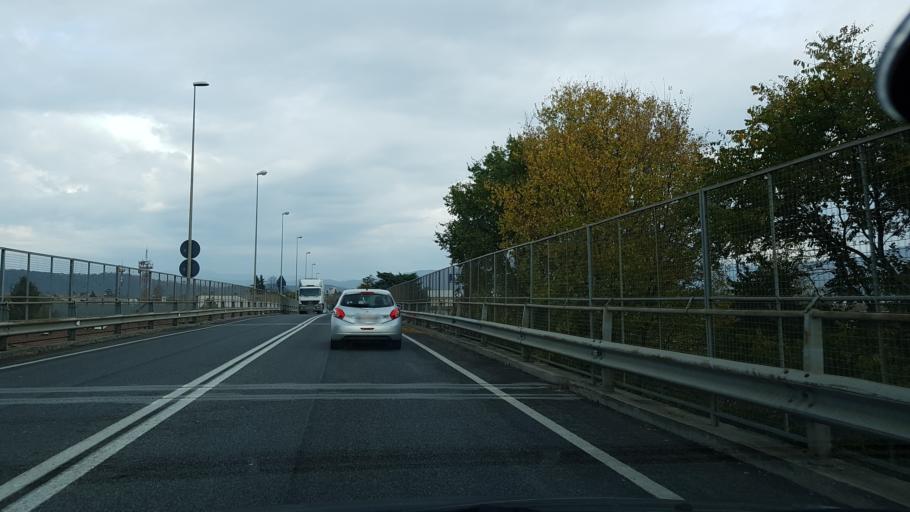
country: SI
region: Sempeter-Vrtojba
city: Vrtojba
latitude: 45.9202
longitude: 13.6136
